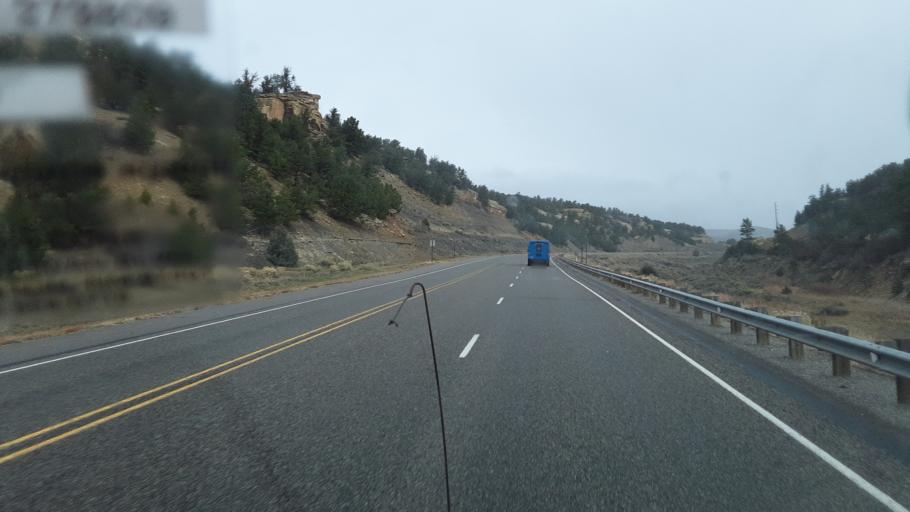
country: US
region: New Mexico
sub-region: Rio Arriba County
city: Tierra Amarilla
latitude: 36.4272
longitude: -106.4787
